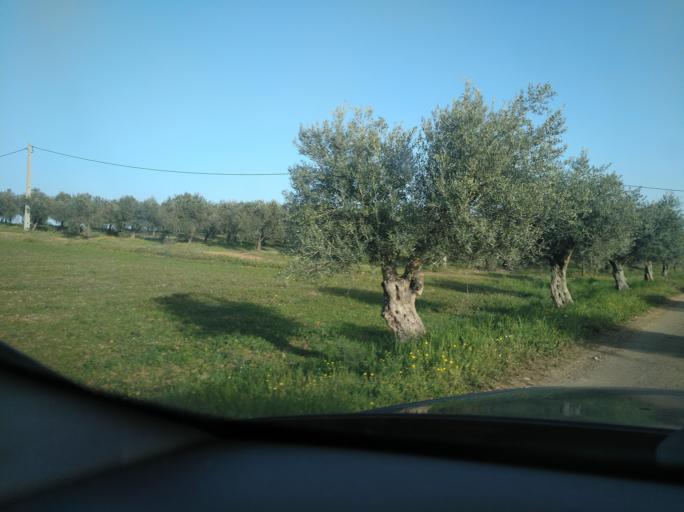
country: PT
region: Portalegre
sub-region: Campo Maior
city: Campo Maior
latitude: 39.0123
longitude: -7.0369
